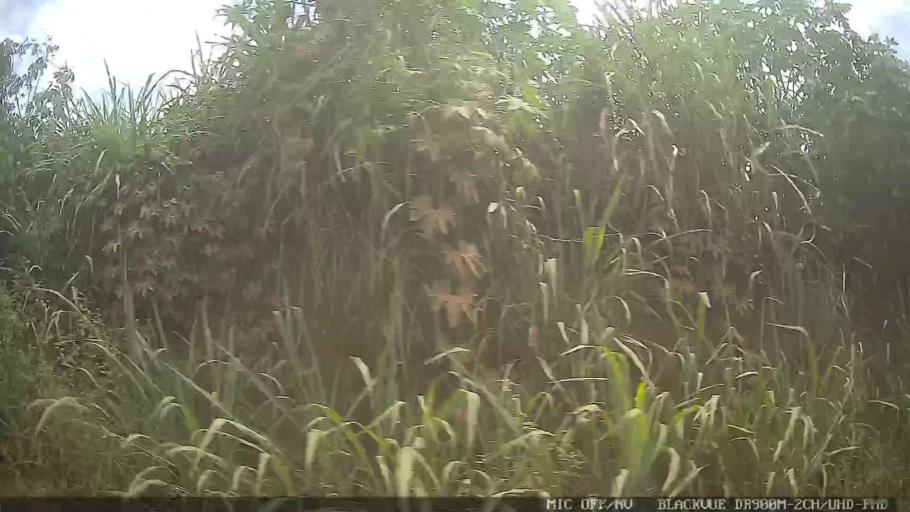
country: BR
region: Sao Paulo
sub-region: Atibaia
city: Atibaia
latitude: -23.0443
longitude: -46.5183
